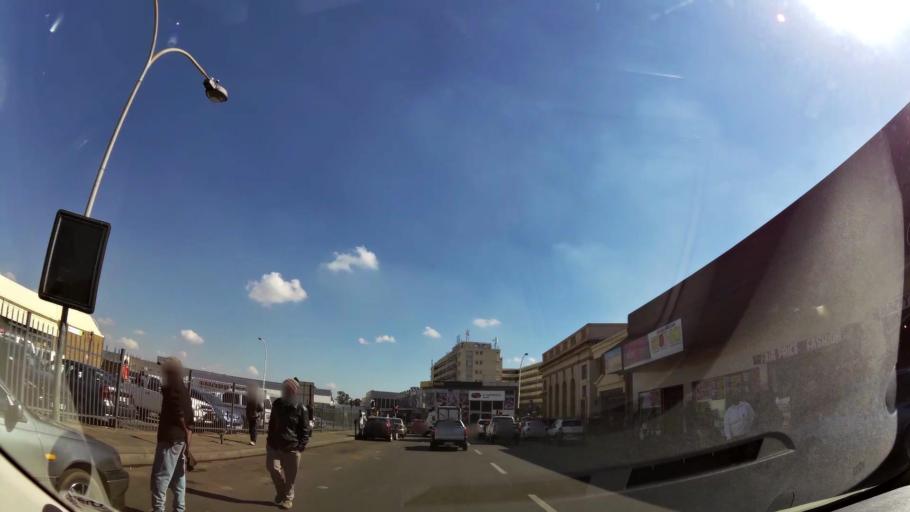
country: ZA
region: Mpumalanga
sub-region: Nkangala District Municipality
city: Witbank
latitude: -25.8747
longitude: 29.2112
